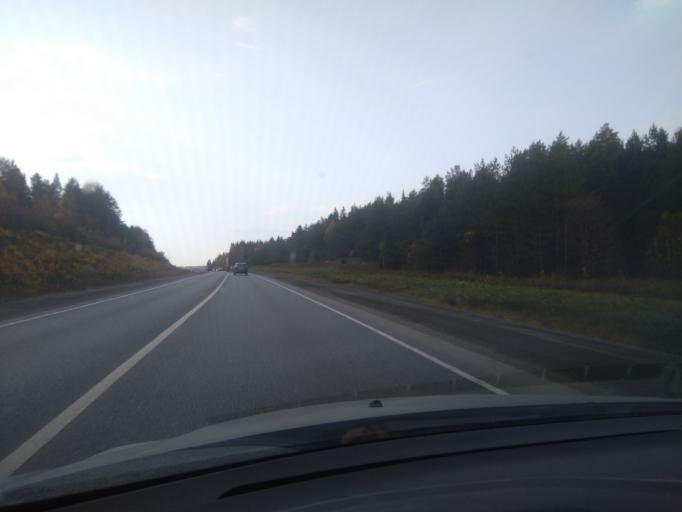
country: RU
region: Sverdlovsk
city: Druzhinino
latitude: 56.8192
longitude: 59.5664
